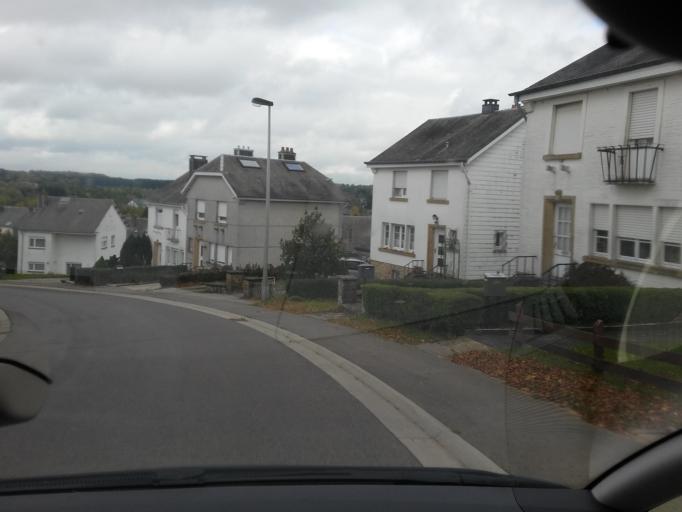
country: BE
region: Wallonia
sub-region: Province du Luxembourg
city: Arlon
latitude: 49.6895
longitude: 5.8042
